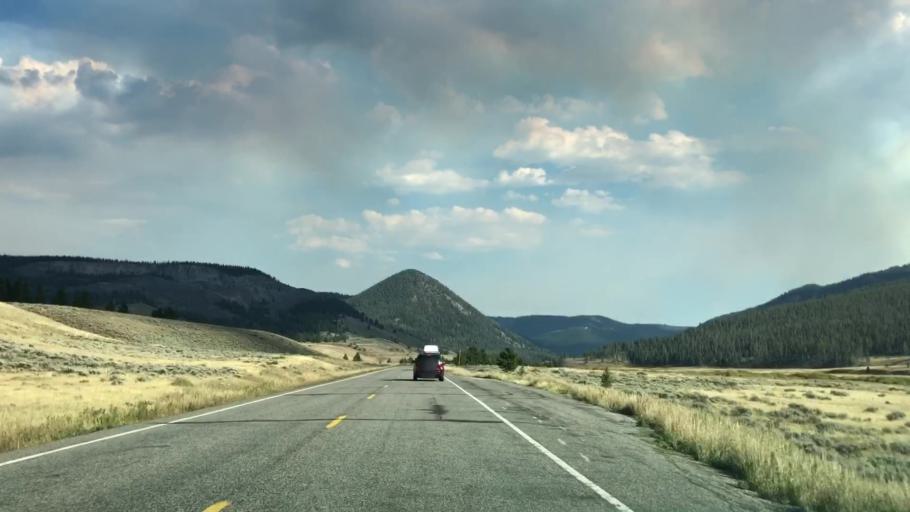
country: US
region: Montana
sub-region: Gallatin County
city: Big Sky
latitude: 45.0504
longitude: -111.1461
